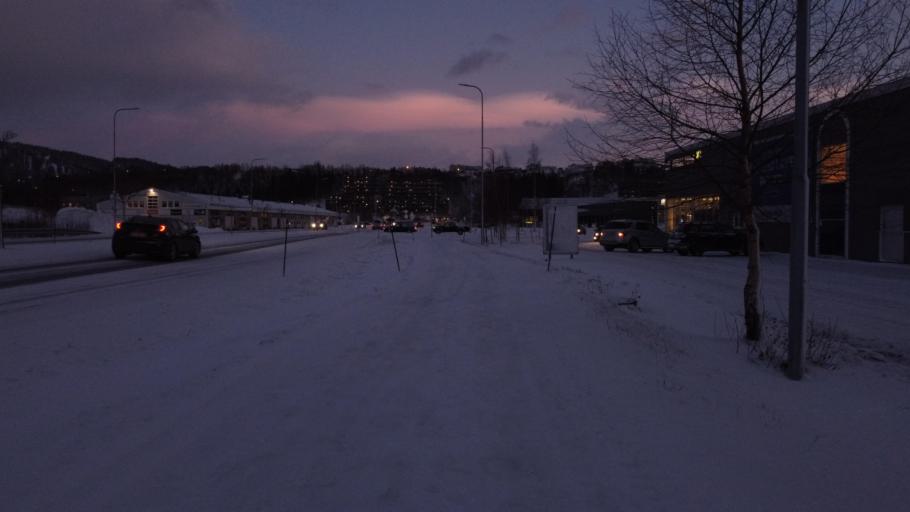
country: NO
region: Nordland
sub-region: Rana
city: Mo i Rana
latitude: 66.3184
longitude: 14.1436
